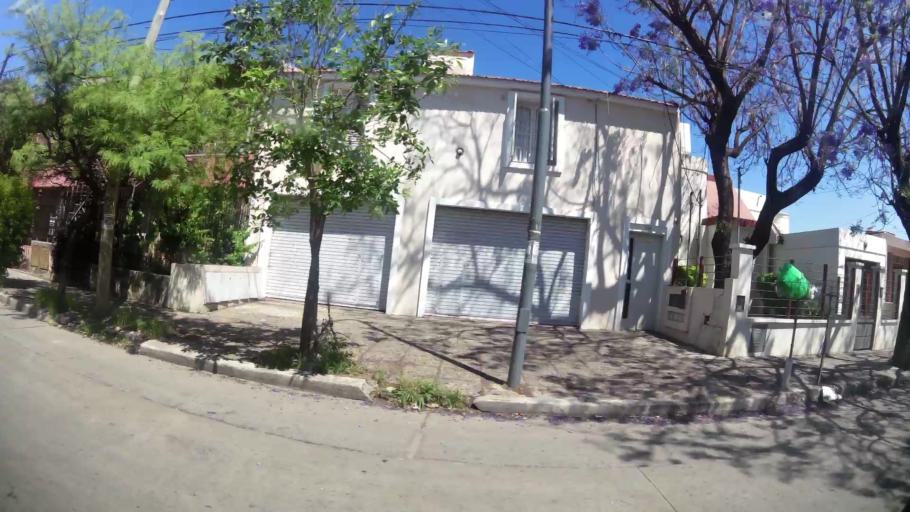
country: AR
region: Cordoba
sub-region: Departamento de Capital
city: Cordoba
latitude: -31.4259
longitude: -64.2099
